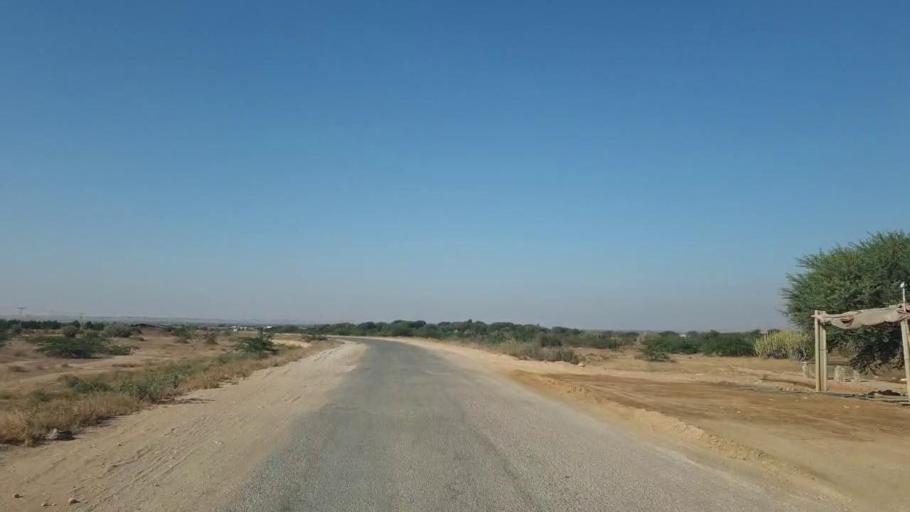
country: PK
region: Sindh
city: Gharo
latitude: 25.1894
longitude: 67.6564
